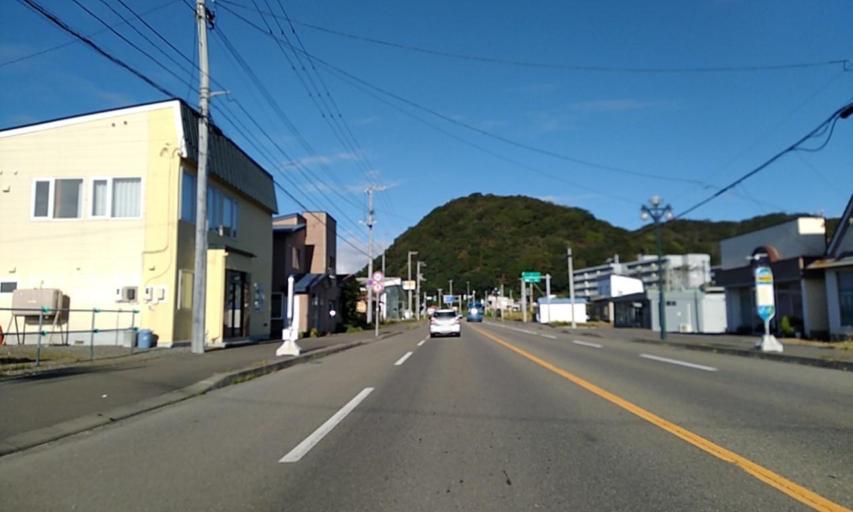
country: JP
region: Hokkaido
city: Shizunai-furukawacho
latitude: 42.1755
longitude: 142.7594
